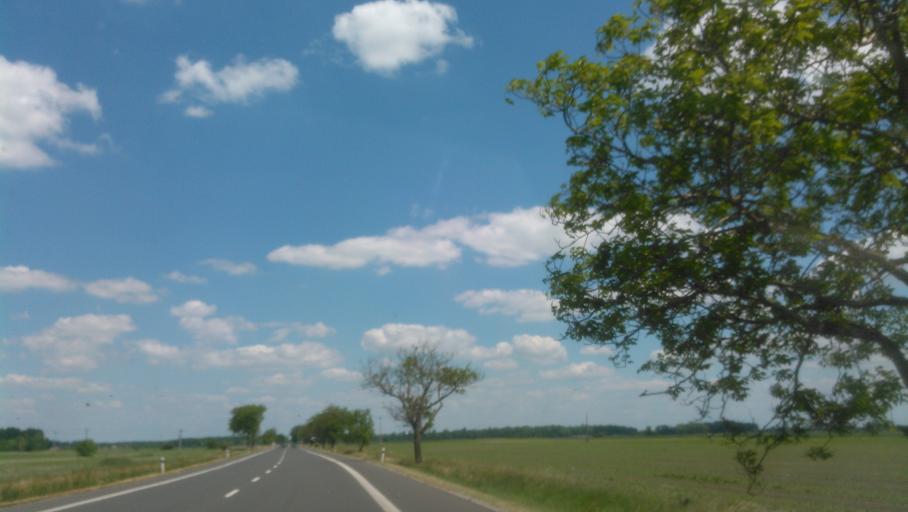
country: SK
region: Trnavsky
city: Dunajska Streda
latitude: 47.9948
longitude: 17.5207
